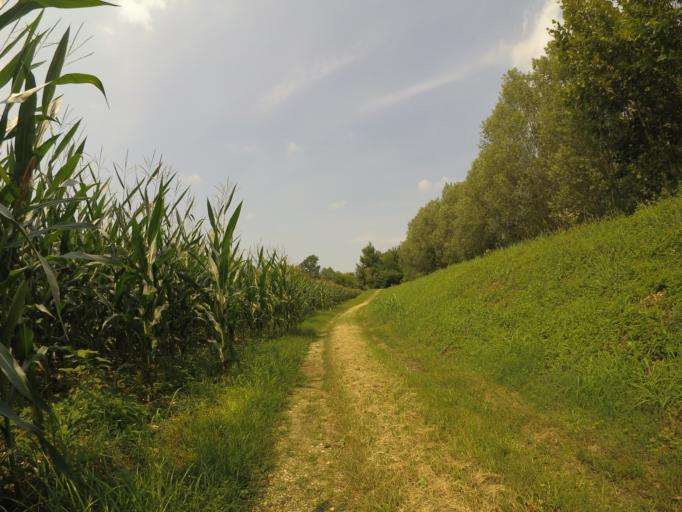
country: IT
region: Friuli Venezia Giulia
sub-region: Provincia di Udine
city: Varmo
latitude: 45.9048
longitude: 13.0197
